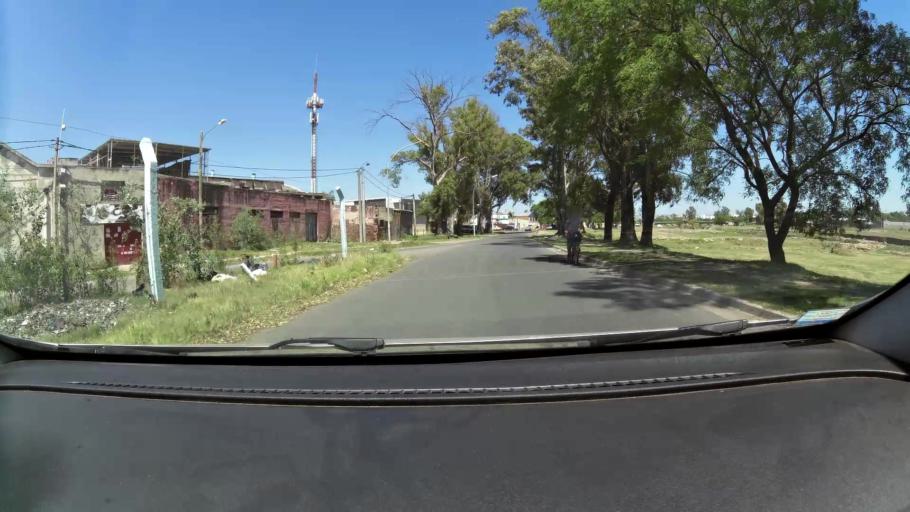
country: AR
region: Cordoba
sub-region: Departamento de Capital
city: Cordoba
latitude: -31.4191
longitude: -64.1457
